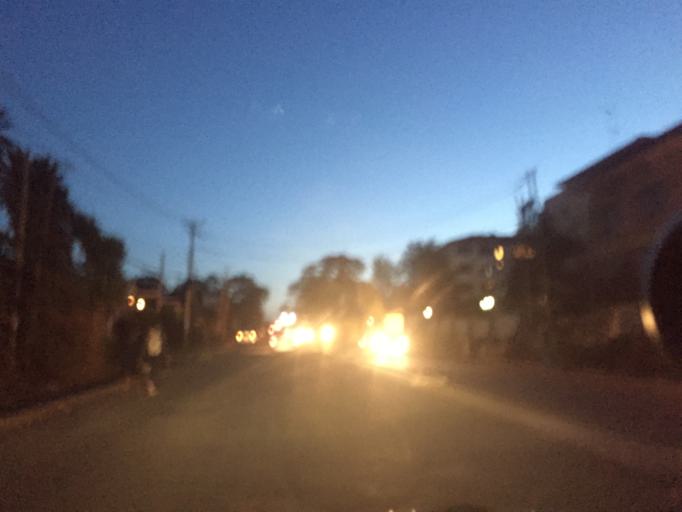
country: KE
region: Nairobi Area
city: Nairobi
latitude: -1.2899
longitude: 36.7616
